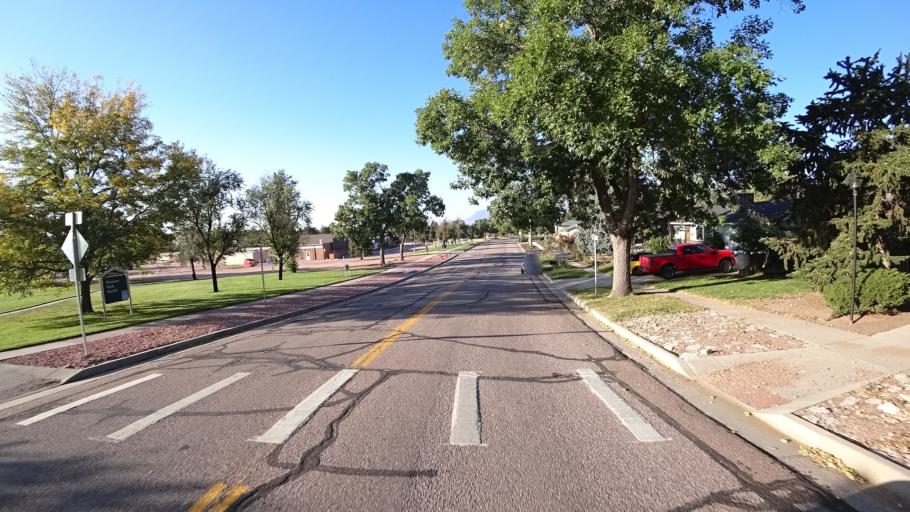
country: US
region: Colorado
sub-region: El Paso County
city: Cimarron Hills
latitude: 38.8798
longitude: -104.7468
